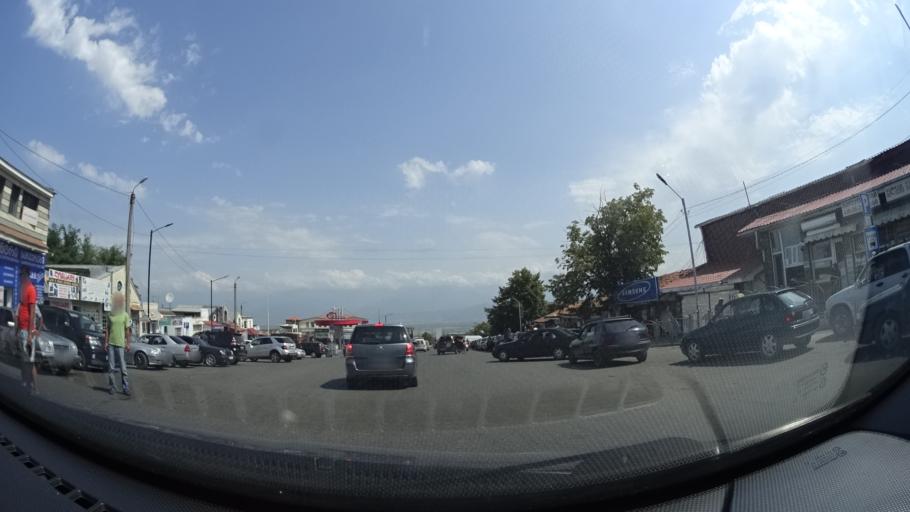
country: GE
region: Kakheti
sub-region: Telavi
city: Telavi
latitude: 41.9222
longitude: 45.4705
